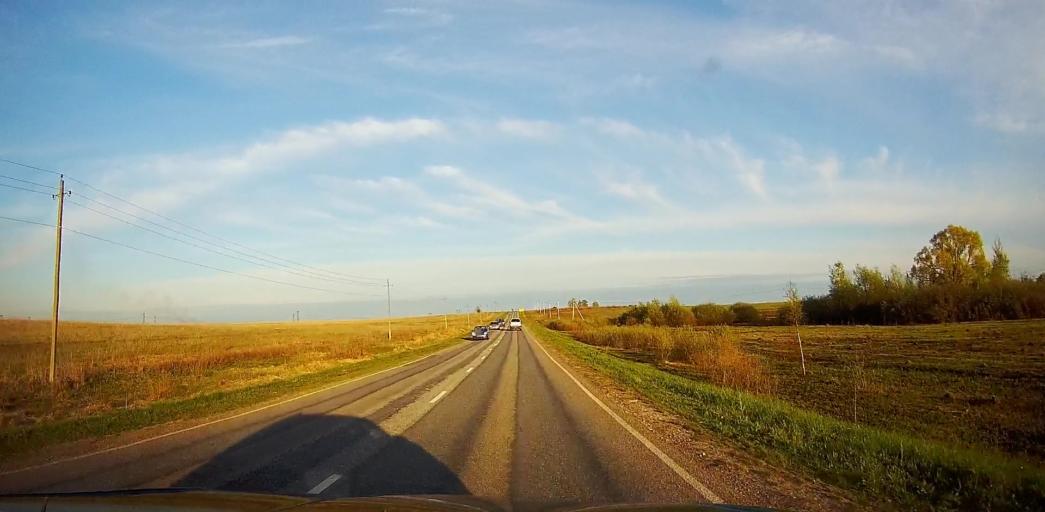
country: RU
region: Moskovskaya
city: Meshcherino
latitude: 55.2707
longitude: 38.2397
